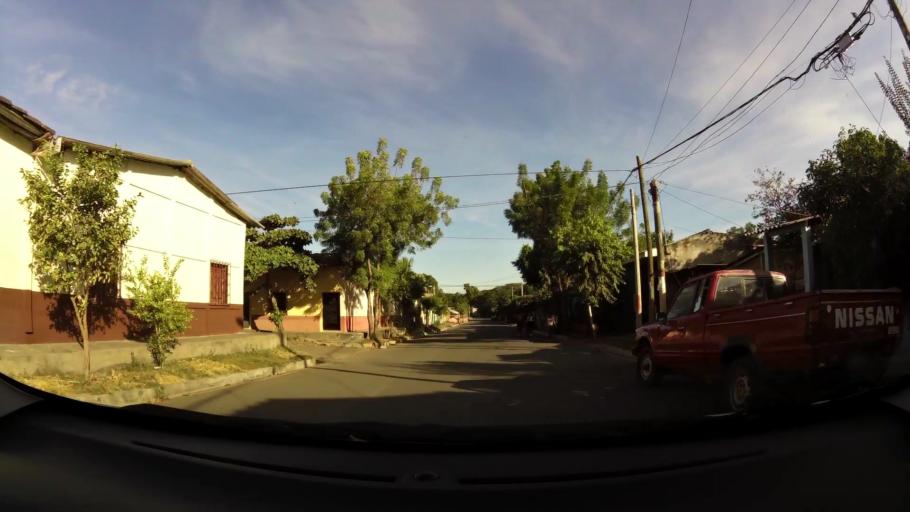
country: SV
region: San Miguel
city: San Miguel
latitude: 13.4627
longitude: -88.1748
